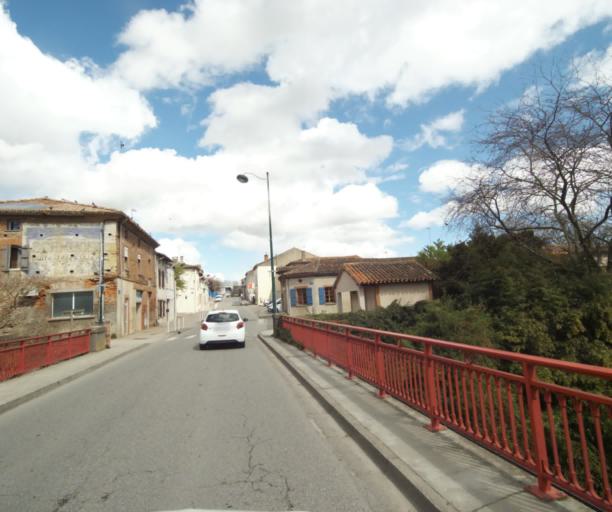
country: FR
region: Midi-Pyrenees
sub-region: Departement de l'Ariege
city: Saverdun
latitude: 43.2322
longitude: 1.5778
